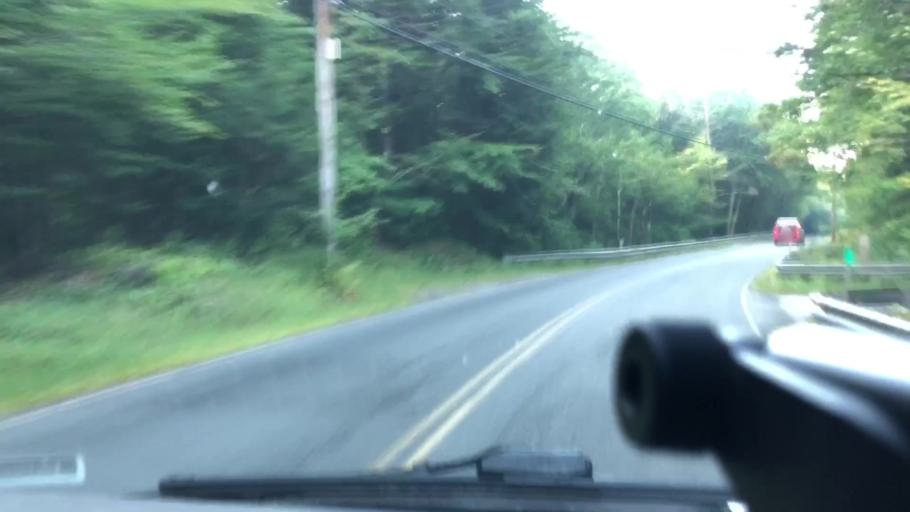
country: US
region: Massachusetts
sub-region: Franklin County
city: Ashfield
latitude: 42.5095
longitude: -72.8231
